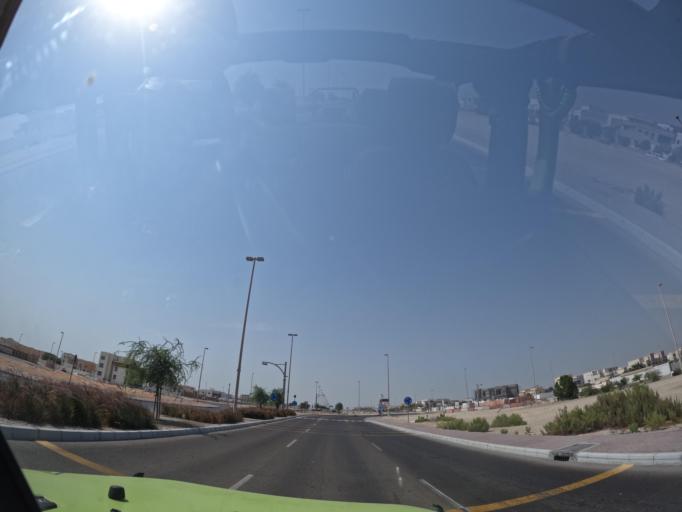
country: AE
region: Abu Dhabi
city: Abu Dhabi
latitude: 24.3497
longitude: 54.6234
